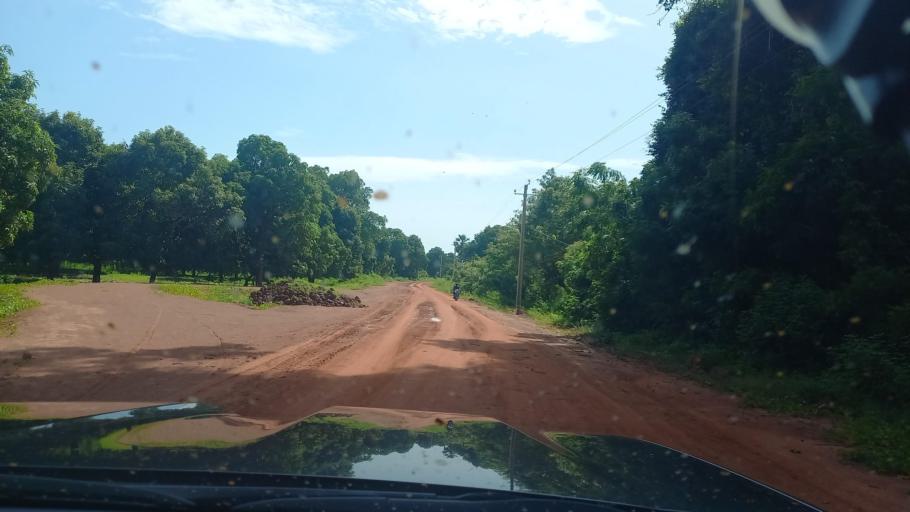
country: SN
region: Ziguinchor
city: Adeane
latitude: 12.6638
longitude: -16.1126
